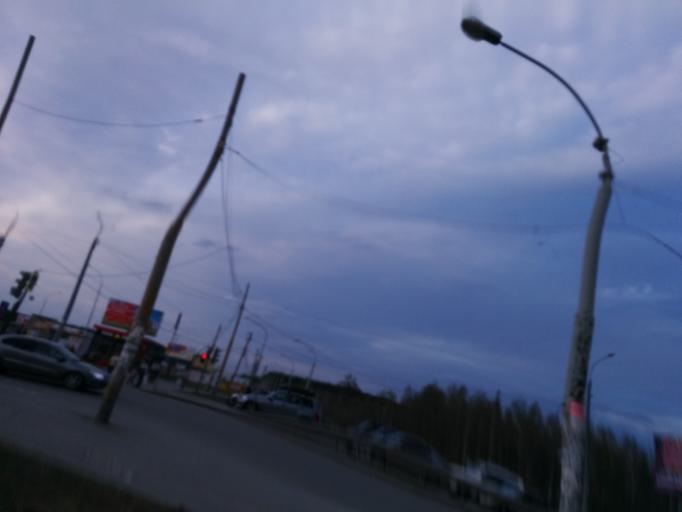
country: RU
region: Sverdlovsk
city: Shirokaya Rechka
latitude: 56.7927
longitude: 60.5216
